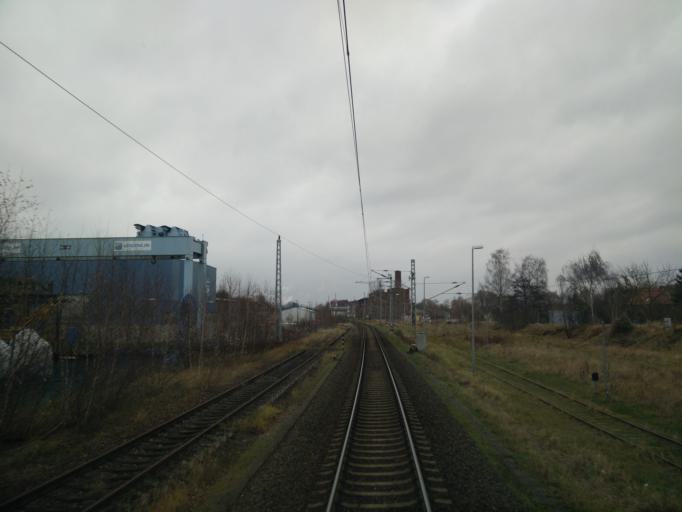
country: DE
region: Mecklenburg-Vorpommern
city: Wismar
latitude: 53.8885
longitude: 11.4759
